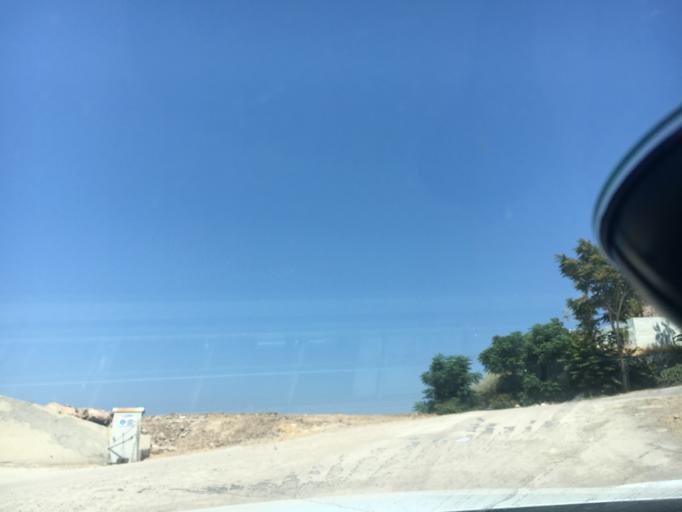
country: TR
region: Canakkale
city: Gulpinar
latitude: 39.4782
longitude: 26.0646
